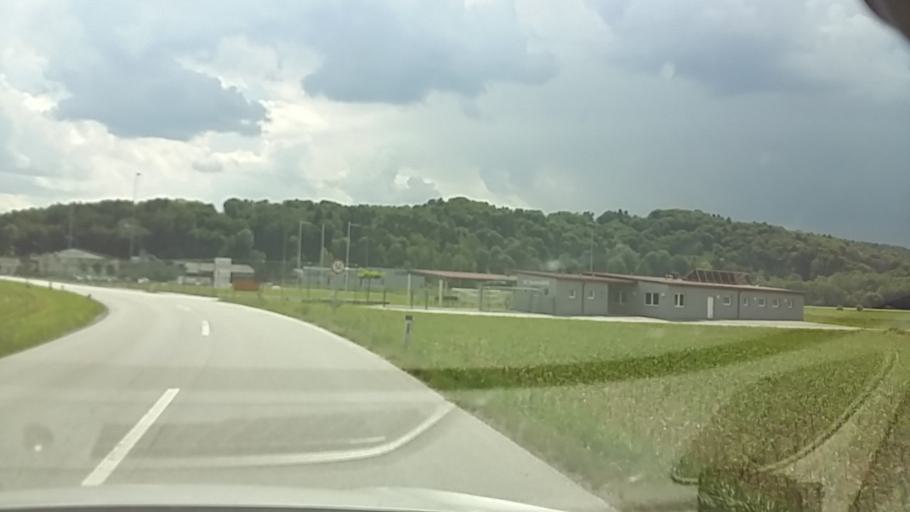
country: AT
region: Styria
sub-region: Politischer Bezirk Suedoststeiermark
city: Breitenfeld an der Rittschein
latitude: 47.0377
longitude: 15.9611
